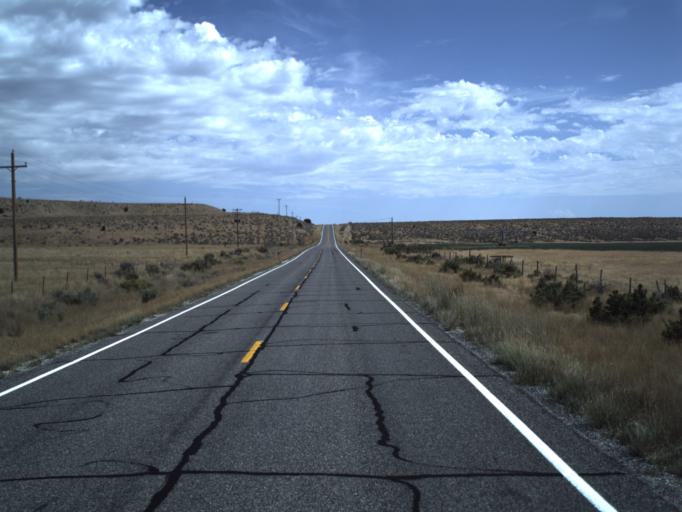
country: US
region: Idaho
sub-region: Cassia County
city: Burley
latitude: 41.8159
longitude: -113.2302
